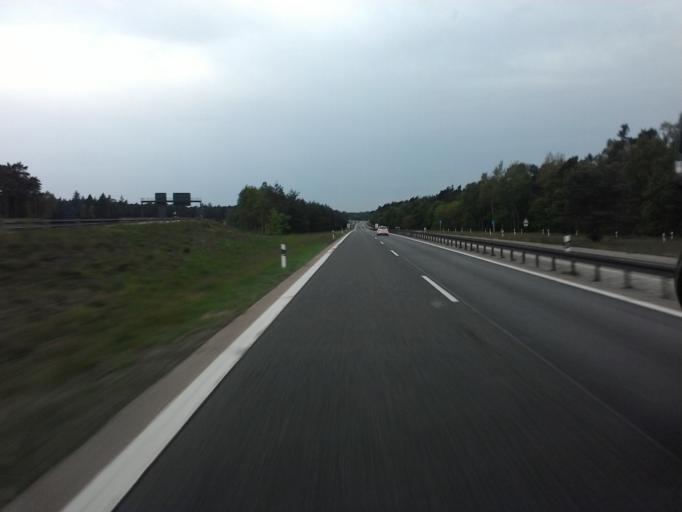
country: DE
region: Bavaria
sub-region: Regierungsbezirk Mittelfranken
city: Rothenbach an der Pegnitz
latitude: 49.4599
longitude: 11.2408
